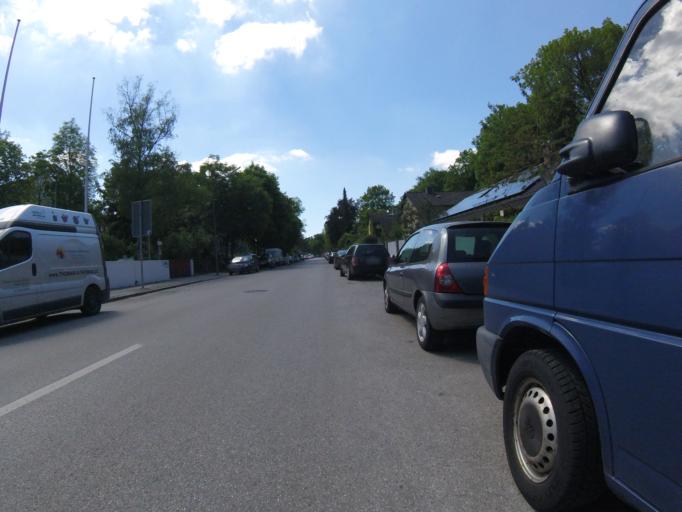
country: DE
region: Bavaria
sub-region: Upper Bavaria
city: Unterhaching
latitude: 48.0919
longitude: 11.6280
